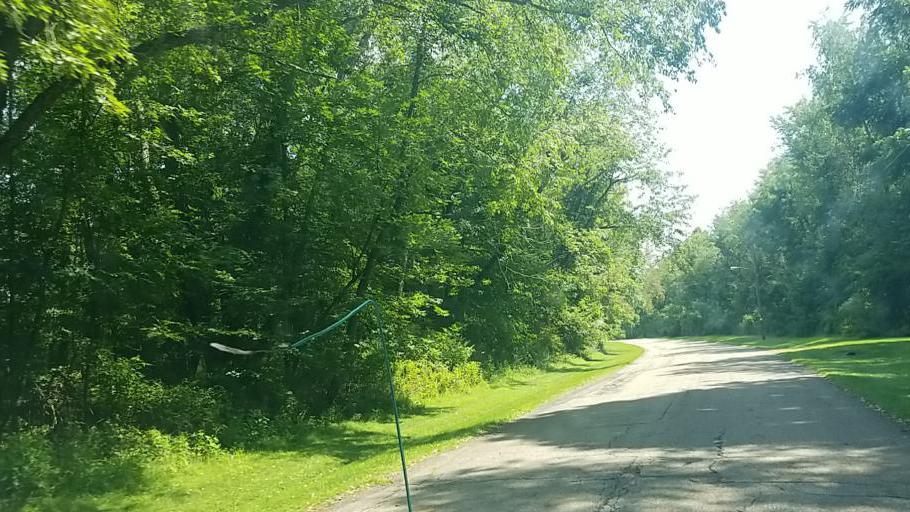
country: US
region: Ohio
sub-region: Sandusky County
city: Bellville
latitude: 40.5915
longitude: -82.4206
